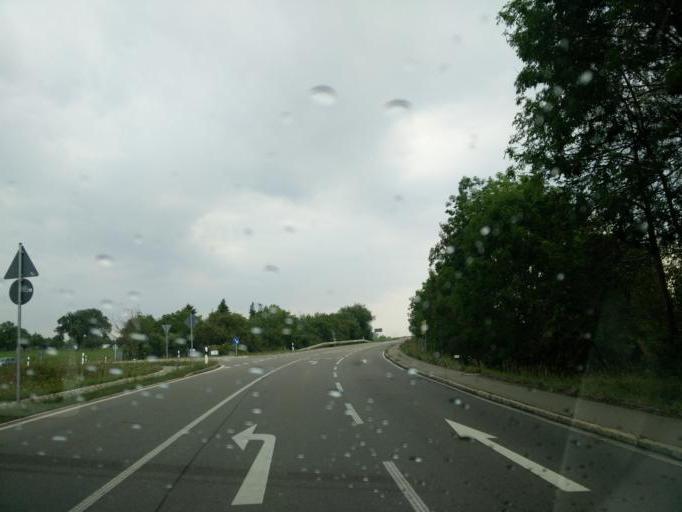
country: DE
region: Baden-Wuerttemberg
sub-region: Tuebingen Region
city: Kusterdingen
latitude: 48.5408
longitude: 9.0922
